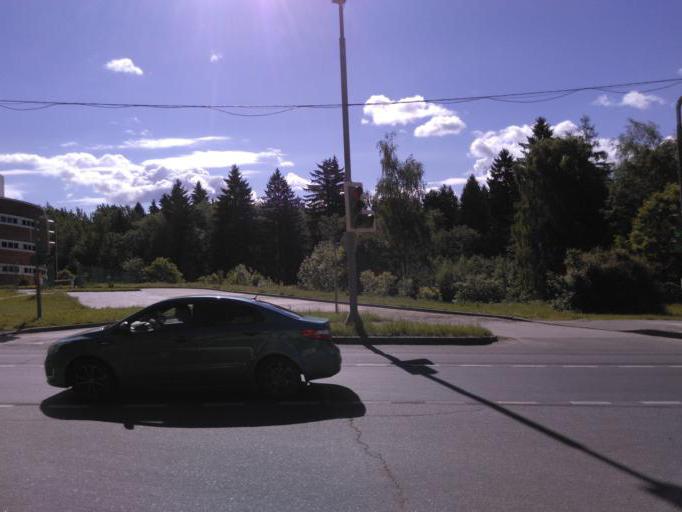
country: RU
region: Moscow
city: Zelenograd
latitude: 55.9918
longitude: 37.1865
